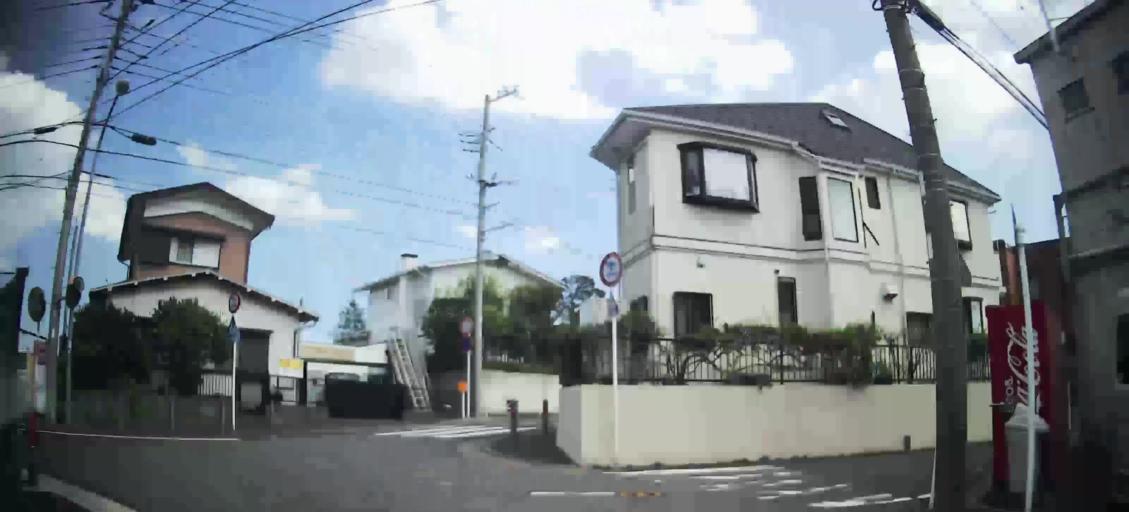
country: JP
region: Kanagawa
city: Yokohama
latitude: 35.4825
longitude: 139.5761
